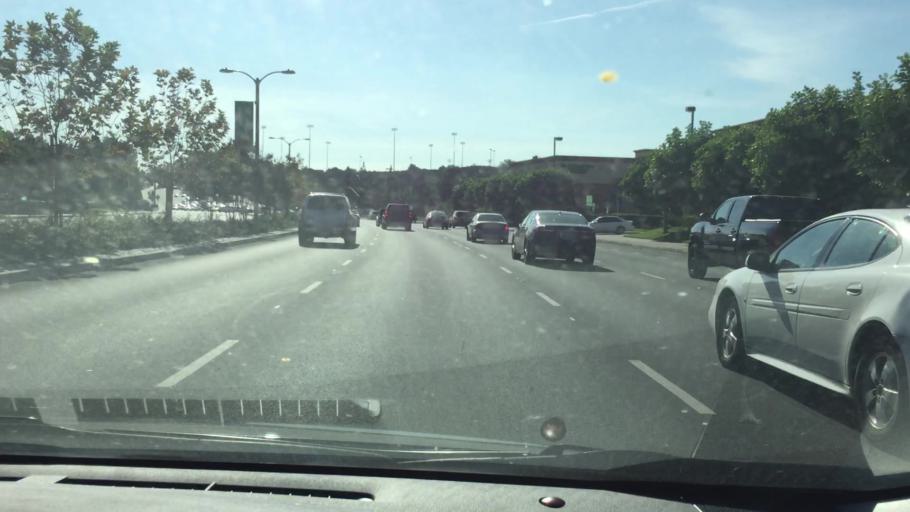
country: US
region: California
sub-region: Orange County
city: Foothill Ranch
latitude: 33.6619
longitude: -117.6533
